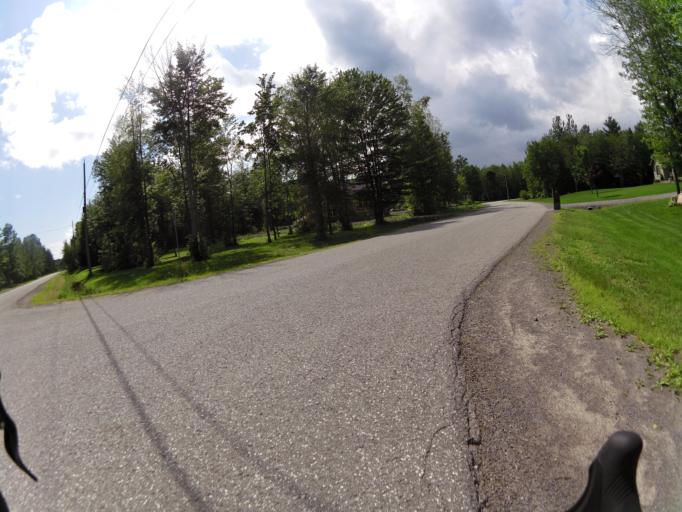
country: CA
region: Ontario
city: Bells Corners
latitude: 45.1707
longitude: -75.8497
